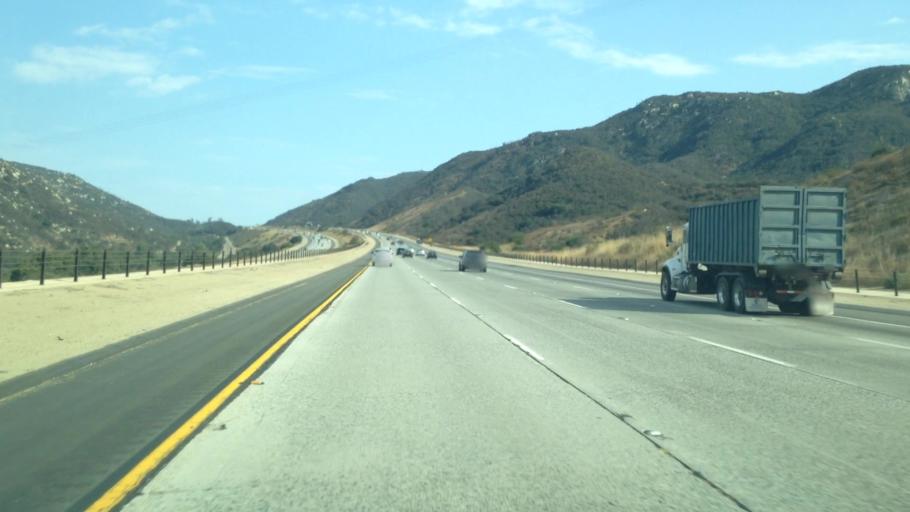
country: US
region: California
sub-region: San Diego County
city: Hidden Meadows
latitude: 33.2270
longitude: -117.1448
